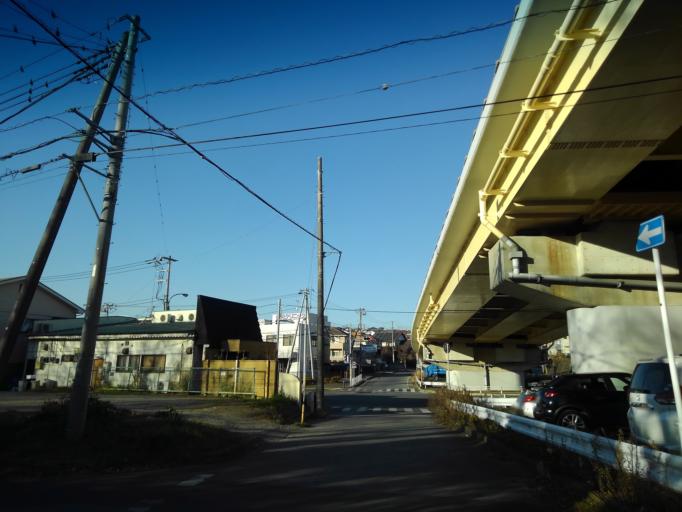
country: JP
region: Chiba
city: Kimitsu
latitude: 35.3320
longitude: 139.9032
